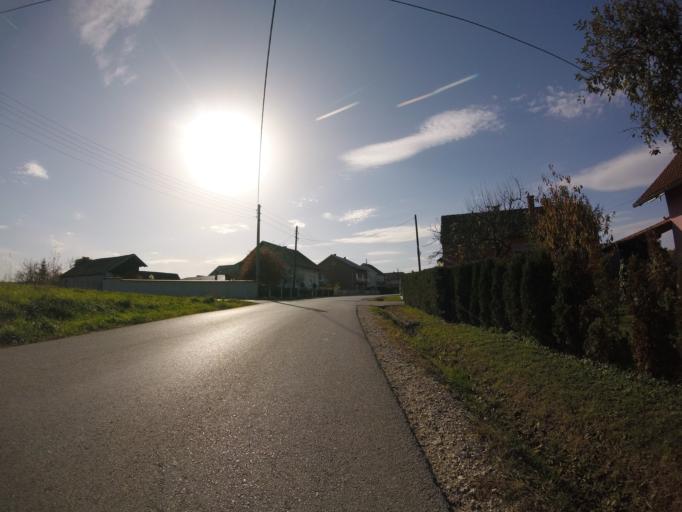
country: HR
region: Zagrebacka
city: Gradici
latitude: 45.6350
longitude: 16.0279
